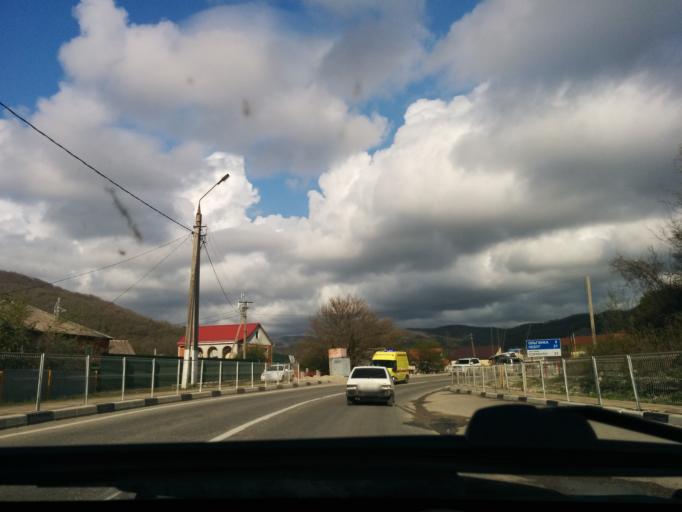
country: RU
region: Krasnodarskiy
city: Novomikhaylovskiy
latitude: 44.2586
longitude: 38.8625
